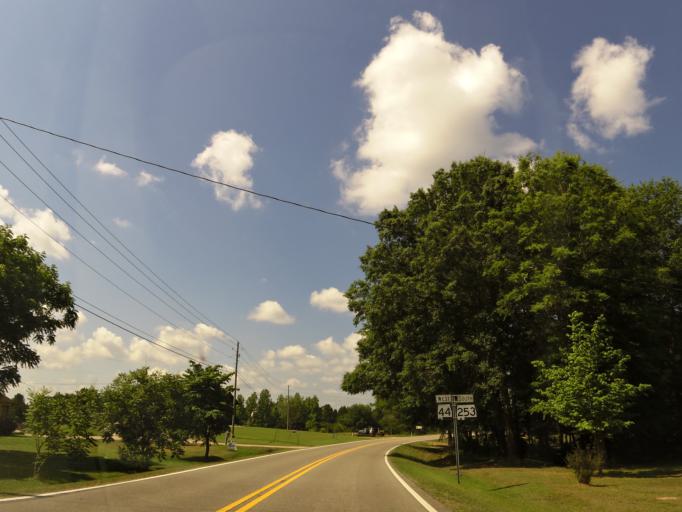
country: US
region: Alabama
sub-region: Marion County
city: Guin
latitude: 34.0076
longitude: -87.8539
